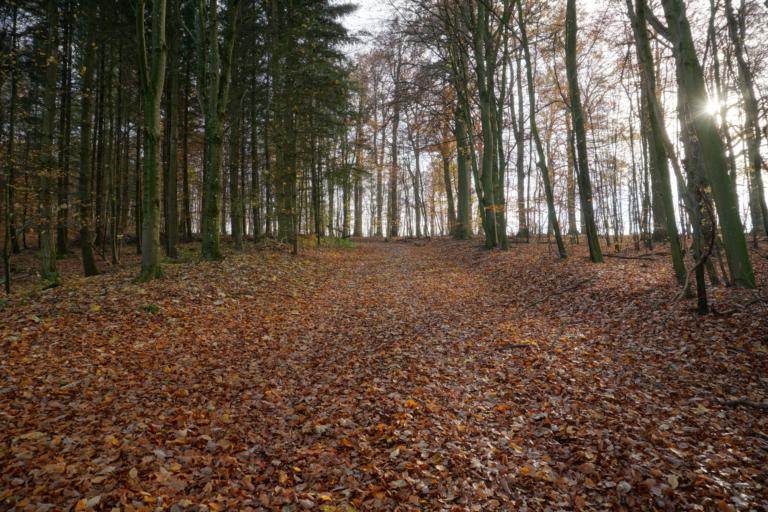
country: DE
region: Baden-Wuerttemberg
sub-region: Karlsruhe Region
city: Binau
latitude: 49.3247
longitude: 9.0289
